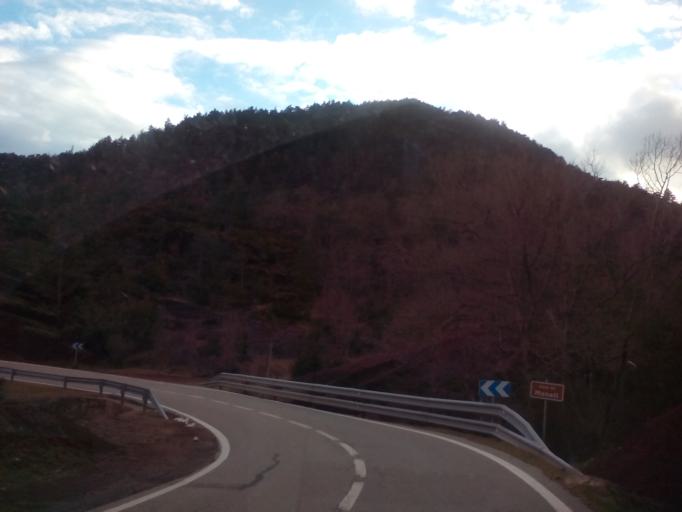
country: ES
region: Catalonia
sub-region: Provincia de Girona
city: Toses
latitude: 42.2739
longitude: 1.9885
